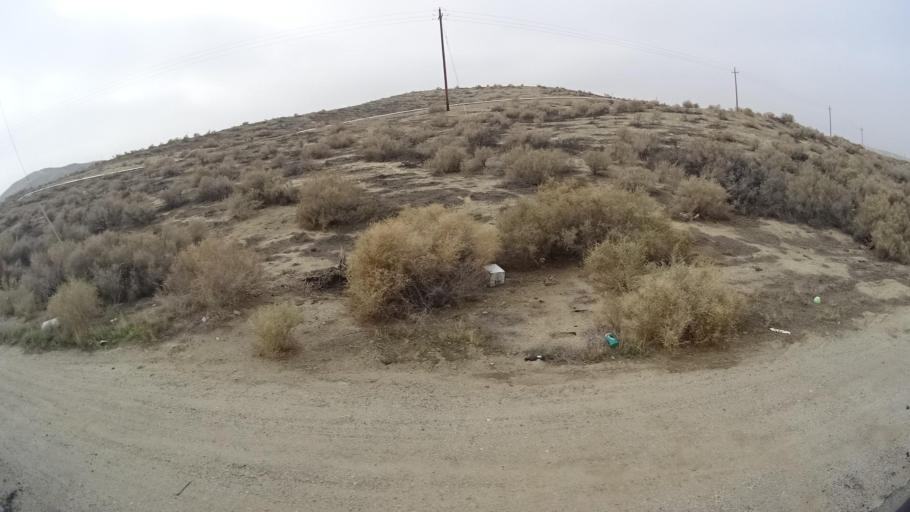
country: US
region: California
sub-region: Kern County
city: Maricopa
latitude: 35.0892
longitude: -119.4004
